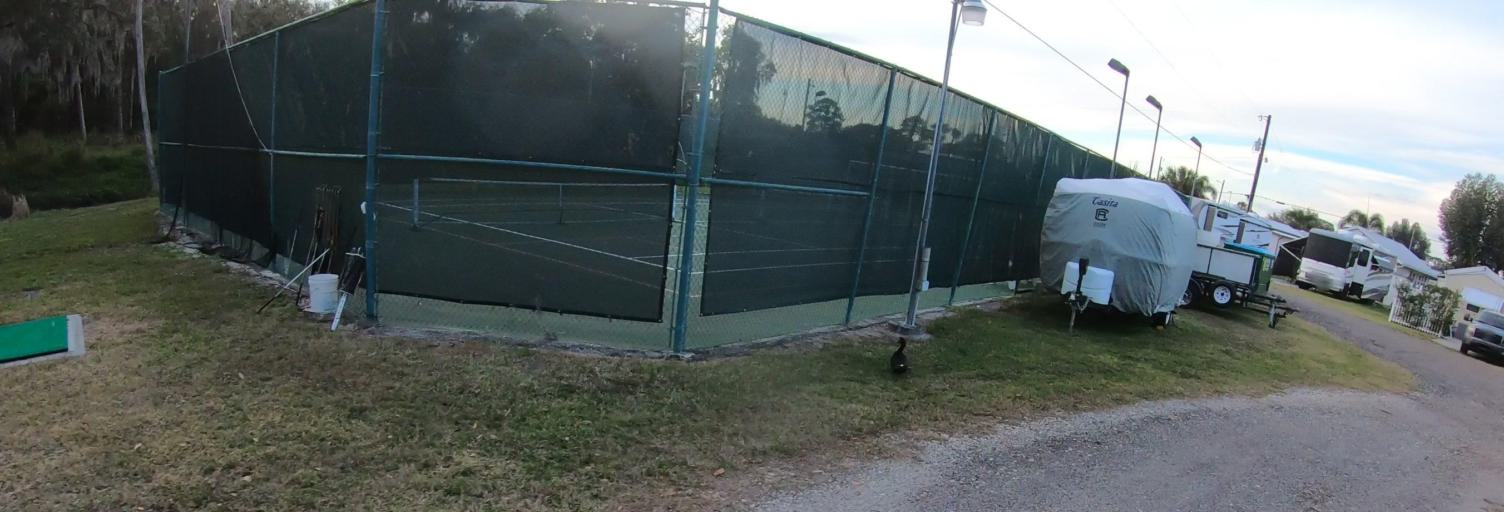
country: US
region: Florida
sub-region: Manatee County
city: Memphis
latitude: 27.5897
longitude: -82.5413
